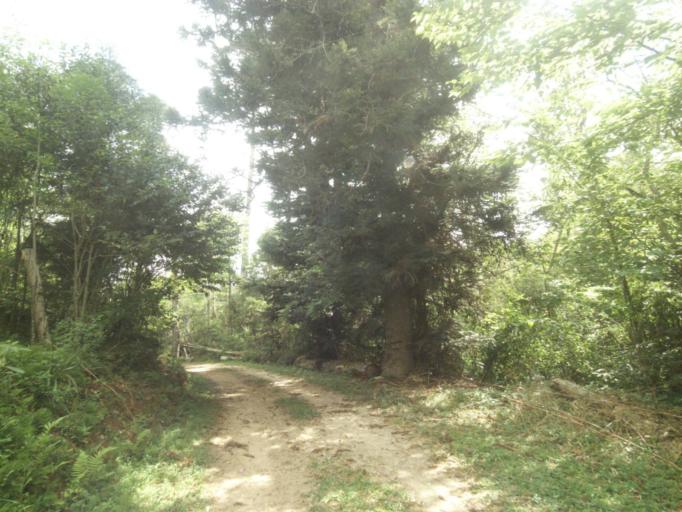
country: BR
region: Parana
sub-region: Almirante Tamandare
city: Almirante Tamandare
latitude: -25.3764
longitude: -49.2955
